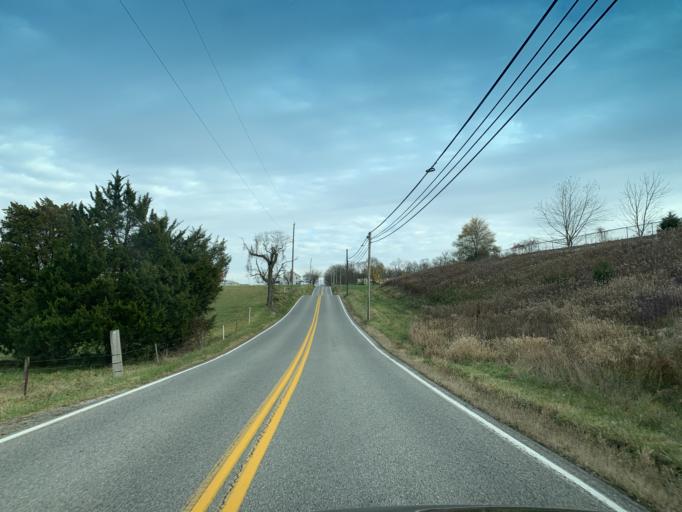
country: US
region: Pennsylvania
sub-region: York County
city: Manchester
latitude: 40.0875
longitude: -76.7594
